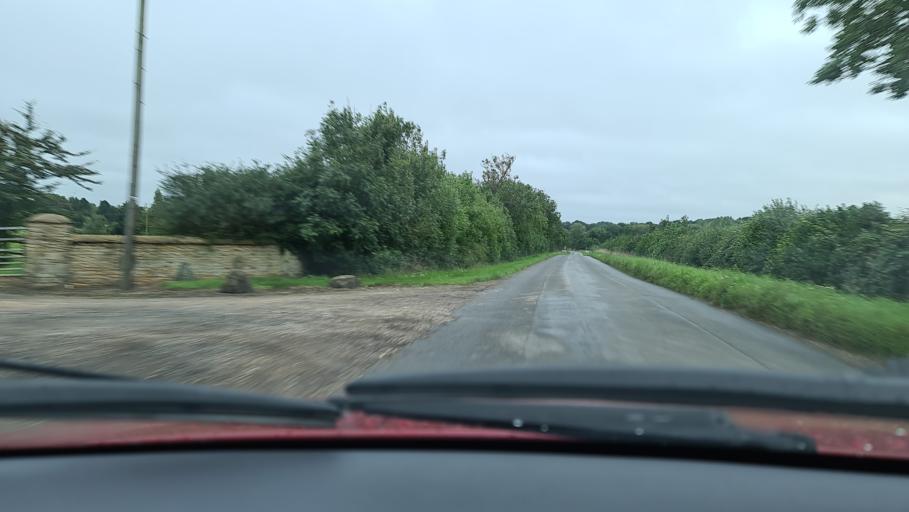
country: GB
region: England
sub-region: Oxfordshire
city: Somerton
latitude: 51.9501
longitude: -1.2215
